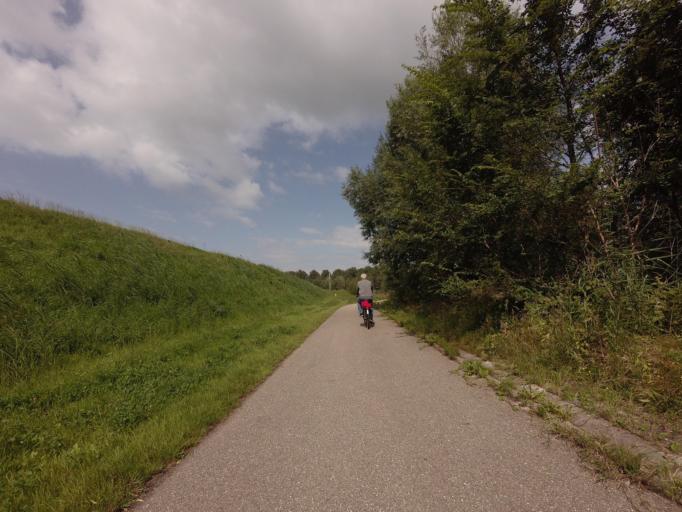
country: NL
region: Flevoland
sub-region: Gemeente Lelystad
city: Lelystad
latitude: 52.5468
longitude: 5.5226
